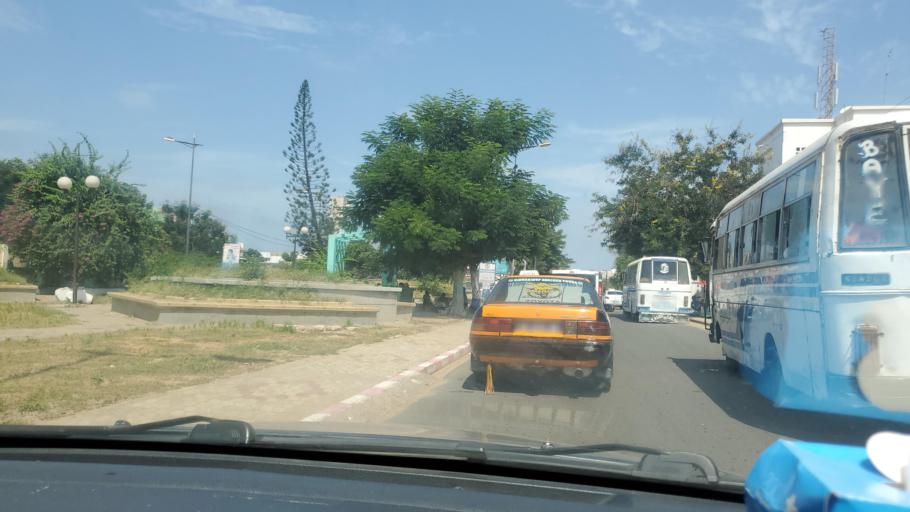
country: SN
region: Dakar
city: Grand Dakar
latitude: 14.7167
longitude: -17.4557
